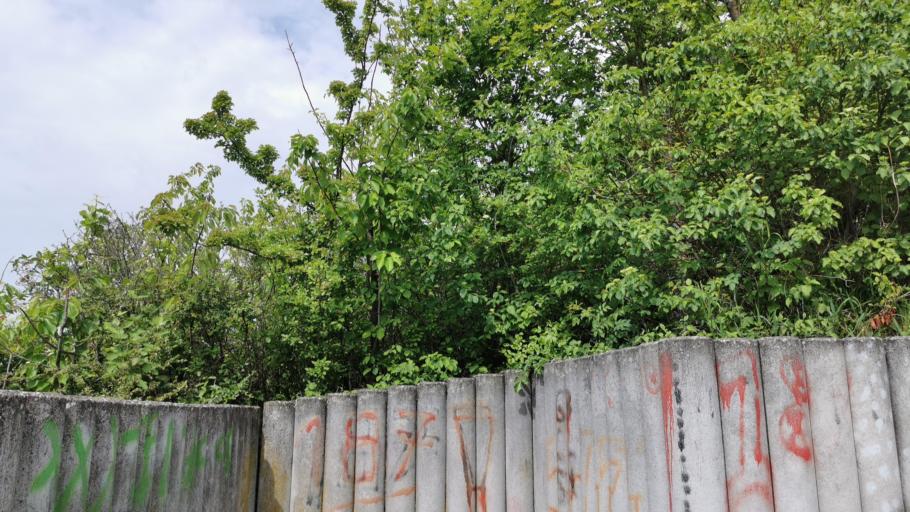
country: DE
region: Baden-Wuerttemberg
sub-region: Regierungsbezirk Stuttgart
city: Leonberg
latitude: 48.7907
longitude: 9.0265
